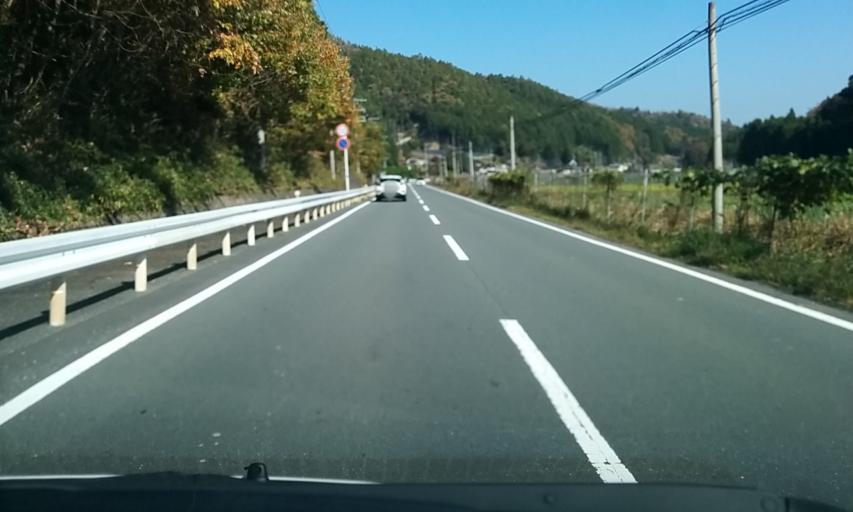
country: JP
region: Kyoto
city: Kameoka
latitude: 35.1991
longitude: 135.5226
